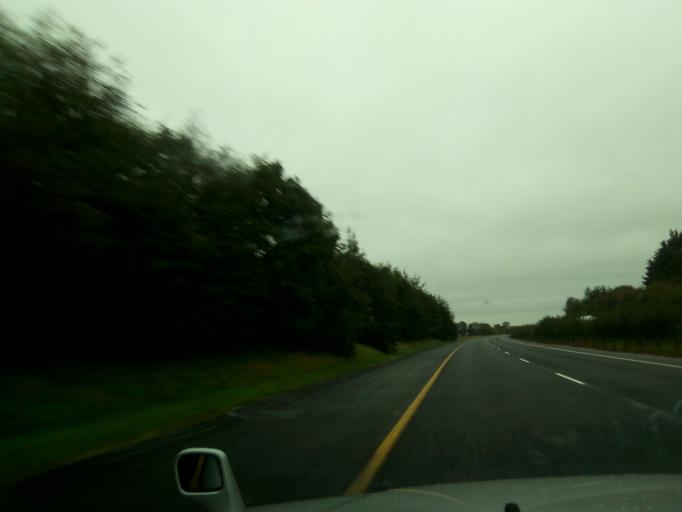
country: IE
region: Leinster
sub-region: An Mhi
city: Enfield
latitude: 53.4073
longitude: -6.7871
